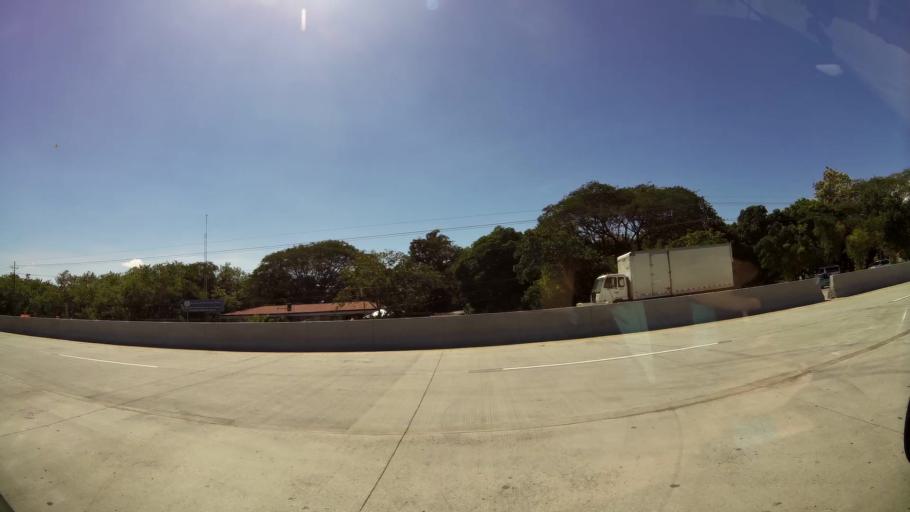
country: CR
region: Guanacaste
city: Liberia
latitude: 10.6237
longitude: -85.4416
